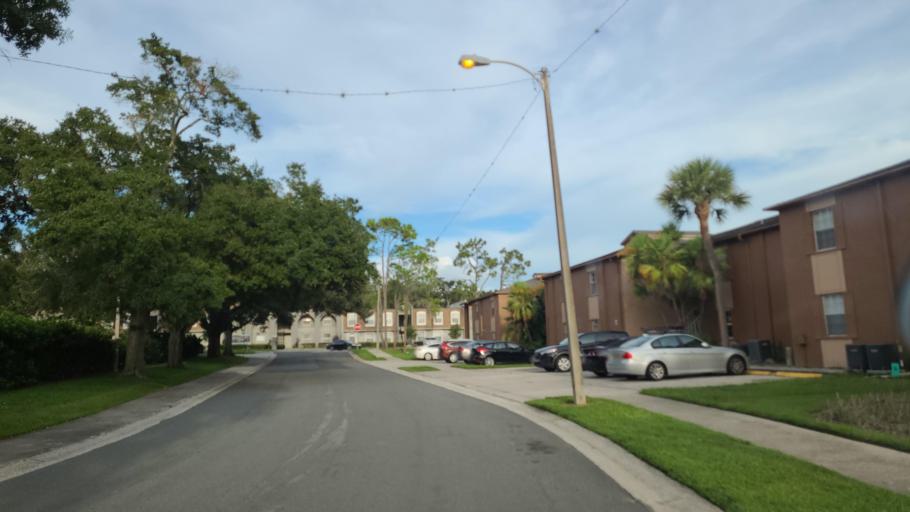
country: US
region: Florida
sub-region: Polk County
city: Lakeland
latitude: 28.0104
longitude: -81.9558
